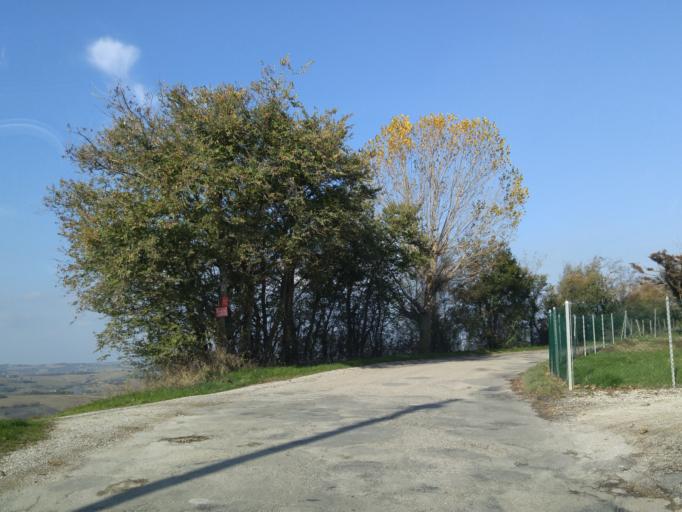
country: IT
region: The Marches
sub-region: Provincia di Pesaro e Urbino
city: Lucrezia
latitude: 43.8049
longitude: 12.9125
